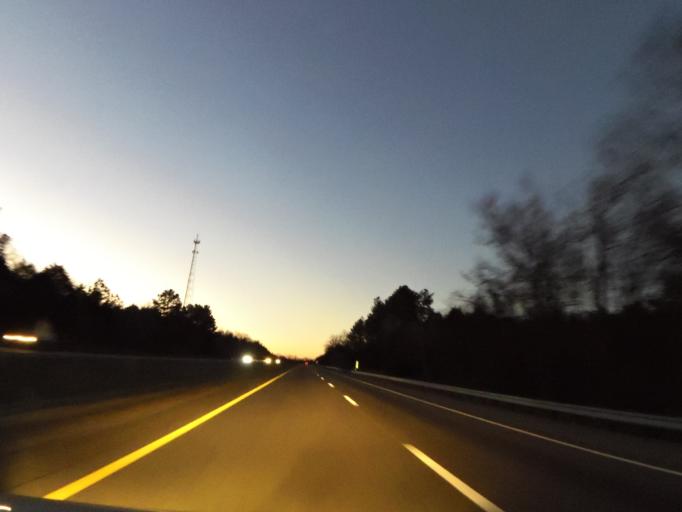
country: US
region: Tennessee
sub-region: Cocke County
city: Newport
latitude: 35.9632
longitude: -83.2170
